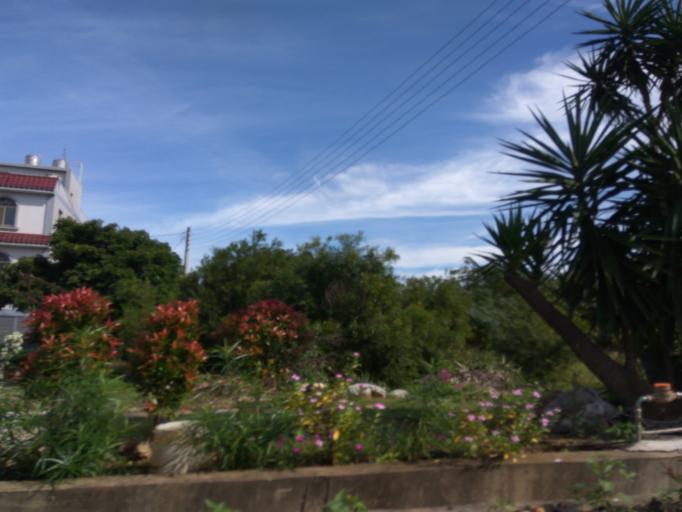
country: TW
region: Taiwan
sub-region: Hsinchu
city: Zhubei
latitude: 25.0175
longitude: 121.0854
